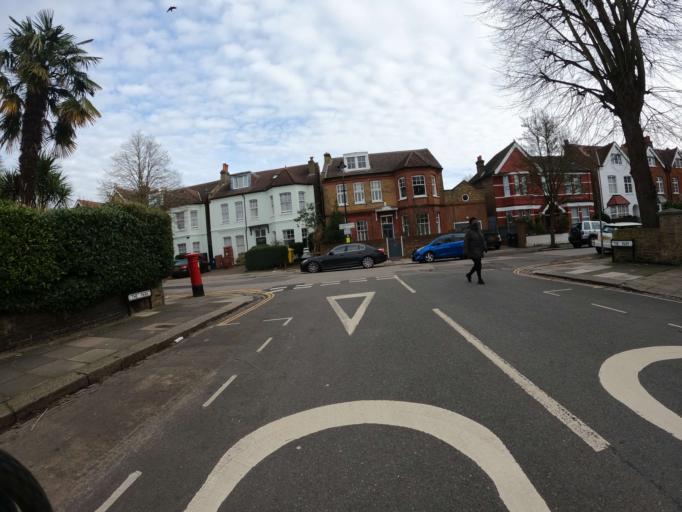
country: GB
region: England
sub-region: Greater London
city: Ealing
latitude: 51.5081
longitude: -0.3002
